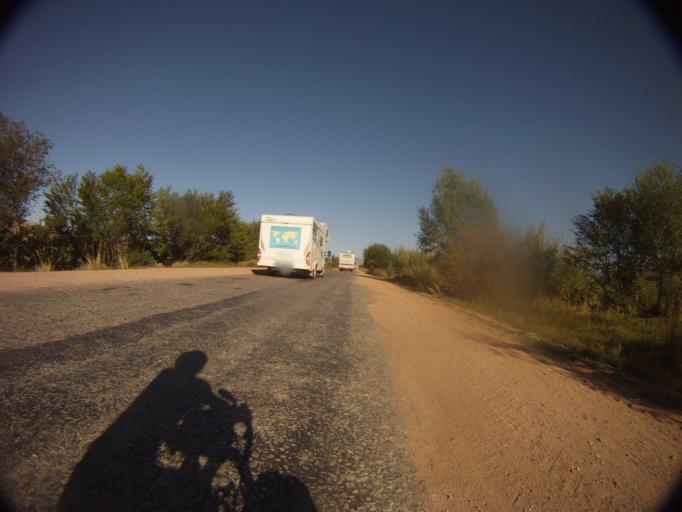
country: KG
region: Ysyk-Koel
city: Bokombayevskoye
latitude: 42.1137
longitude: 76.9316
